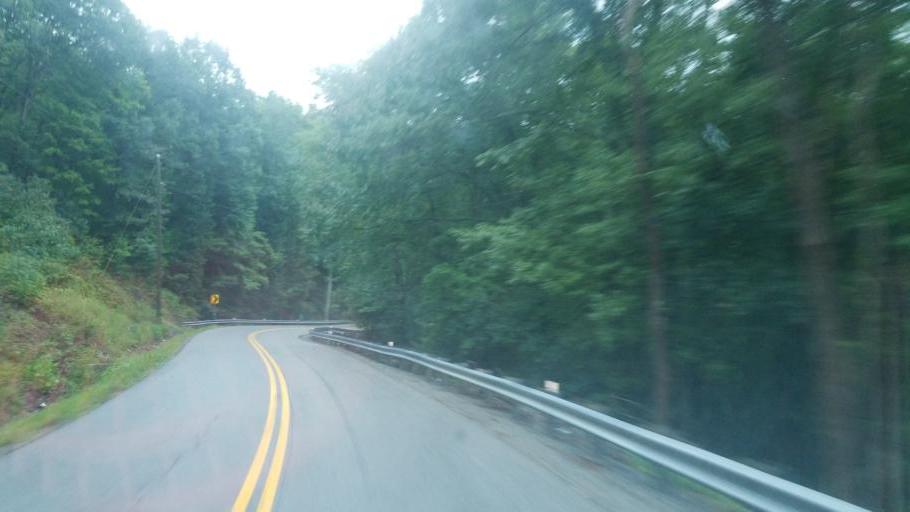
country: US
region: Kentucky
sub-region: Fleming County
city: Flemingsburg
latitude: 38.4052
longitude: -83.5799
